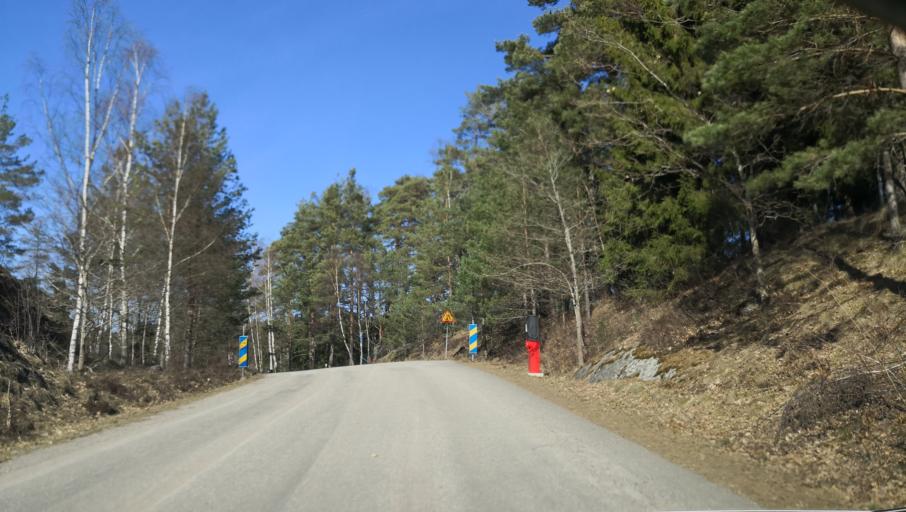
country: SE
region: Stockholm
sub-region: Varmdo Kommun
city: Mortnas
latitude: 59.2956
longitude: 18.4191
